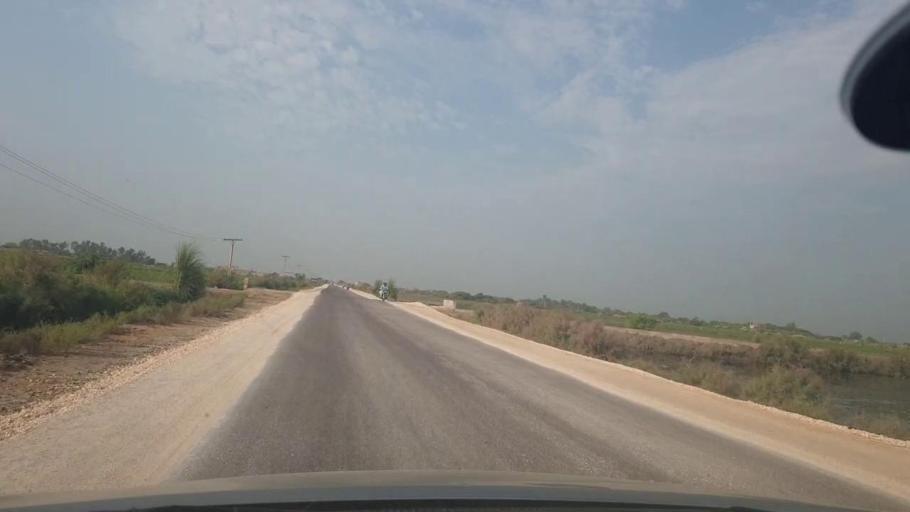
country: PK
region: Sindh
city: Jacobabad
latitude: 28.1435
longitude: 68.3444
